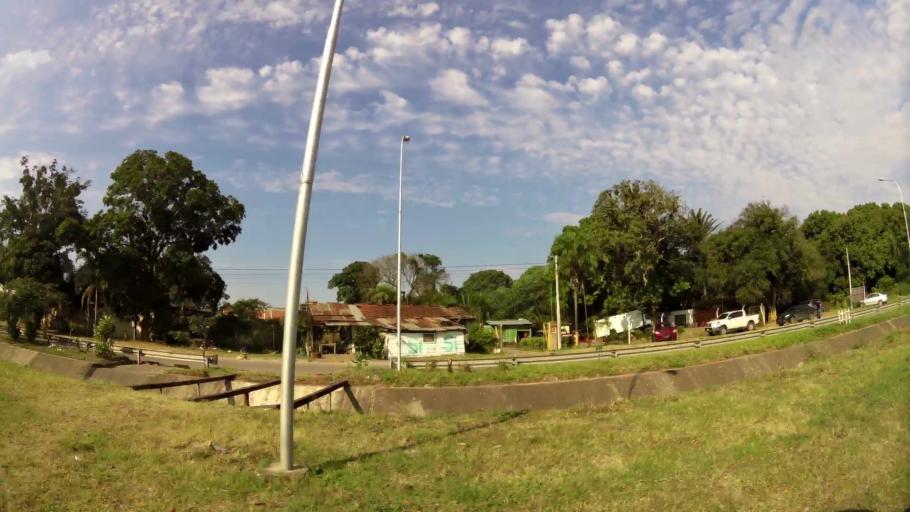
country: BO
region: Santa Cruz
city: Santa Cruz de la Sierra
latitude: -17.7334
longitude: -63.1643
